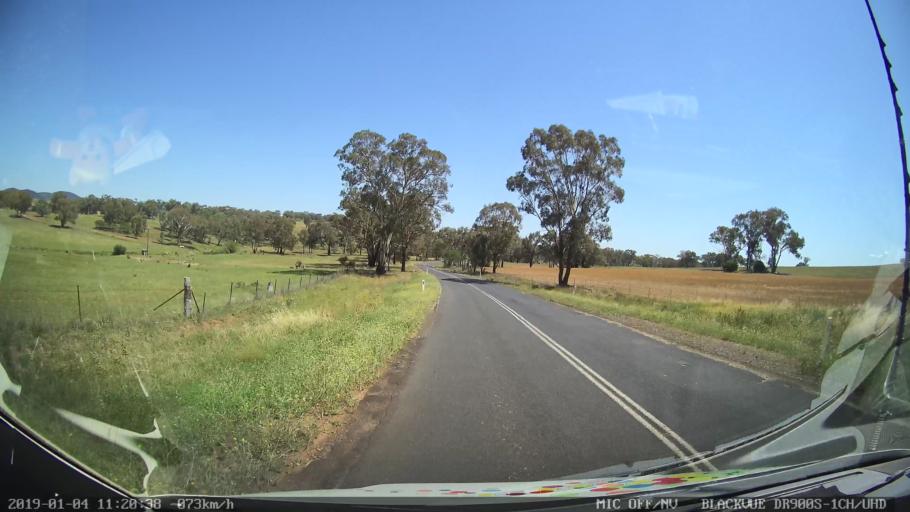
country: AU
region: New South Wales
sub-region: Cabonne
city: Molong
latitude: -33.1619
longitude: 148.7065
